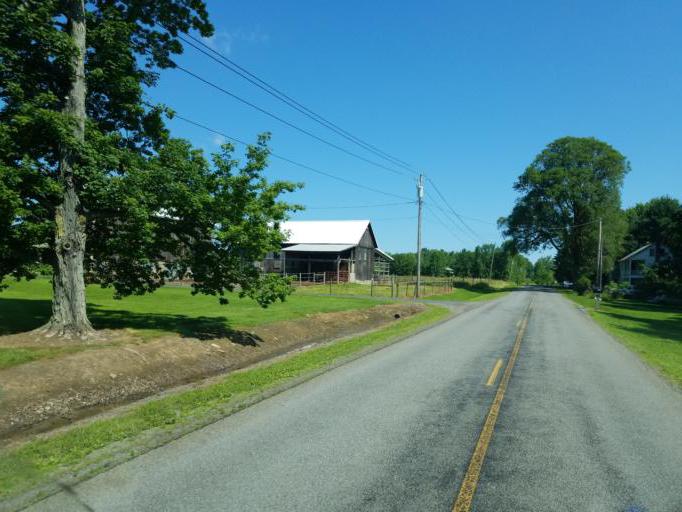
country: US
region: New York
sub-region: Wayne County
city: Wolcott
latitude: 43.2005
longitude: -76.8685
